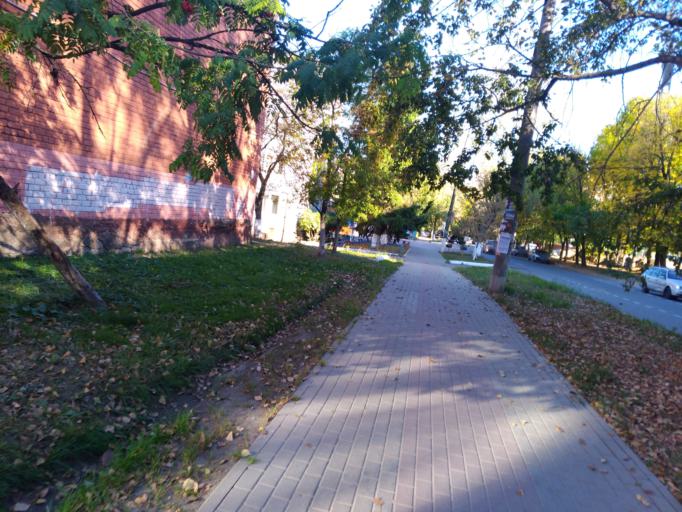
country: RU
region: Kaluga
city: Kaluga
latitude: 54.5171
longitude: 36.2721
